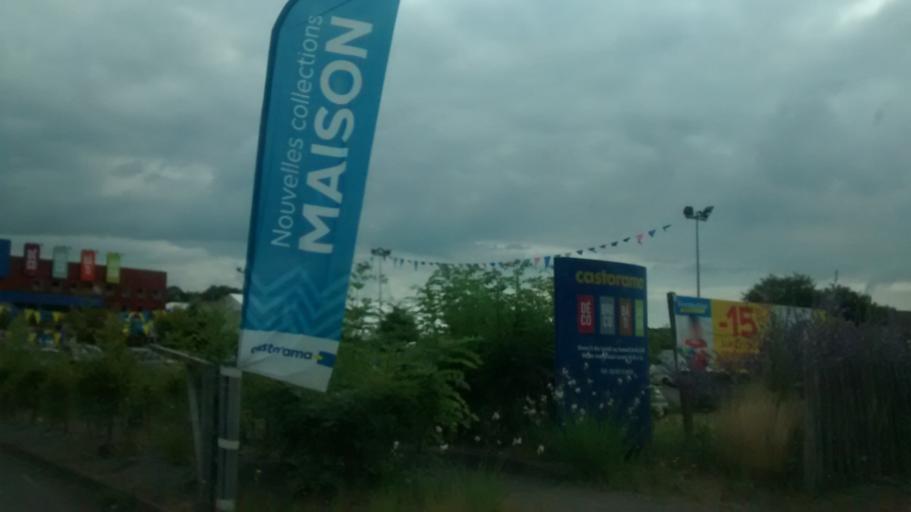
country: FR
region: Brittany
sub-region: Departement d'Ille-et-Vilaine
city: La Chapelle-des-Fougeretz
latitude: 48.2002
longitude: -1.7261
